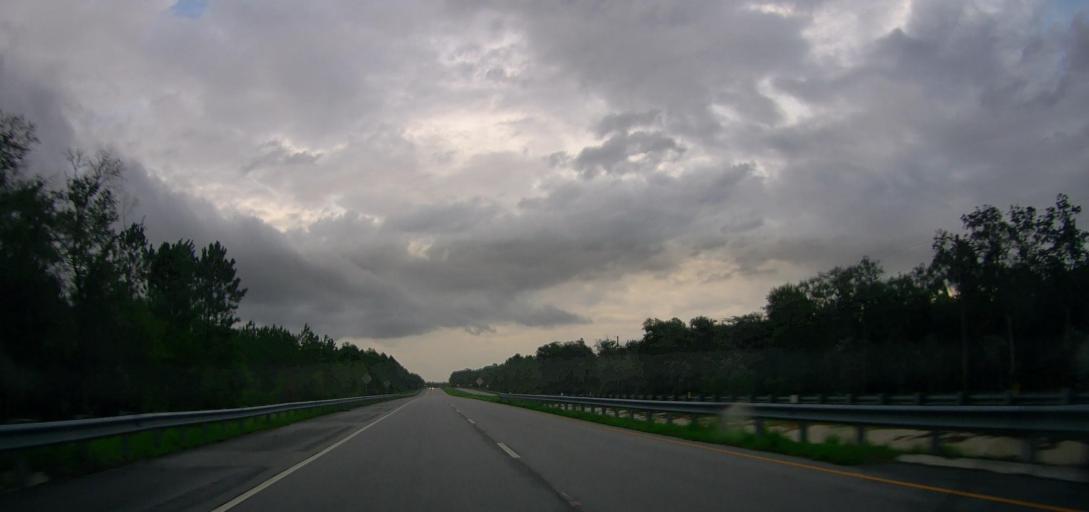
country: US
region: Georgia
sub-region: Ware County
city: Deenwood
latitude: 31.1302
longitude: -82.5136
